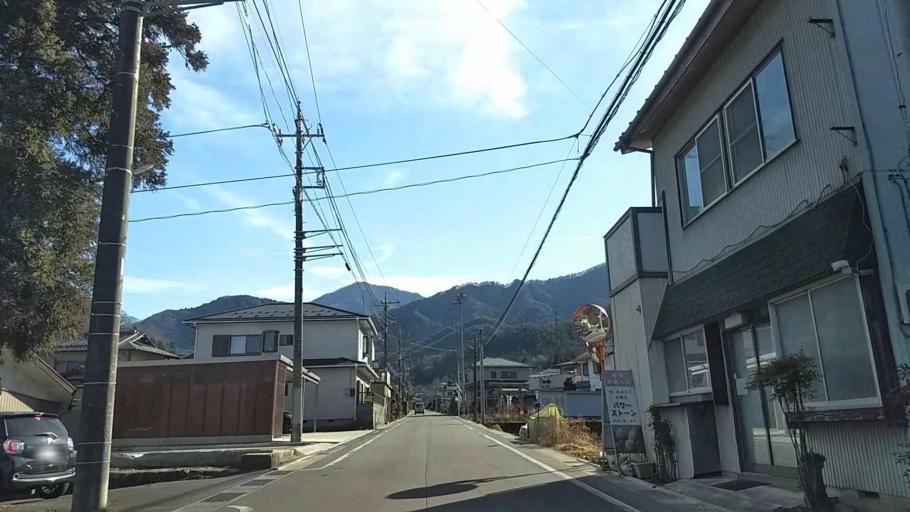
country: JP
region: Yamanashi
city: Otsuki
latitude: 35.5373
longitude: 138.9081
